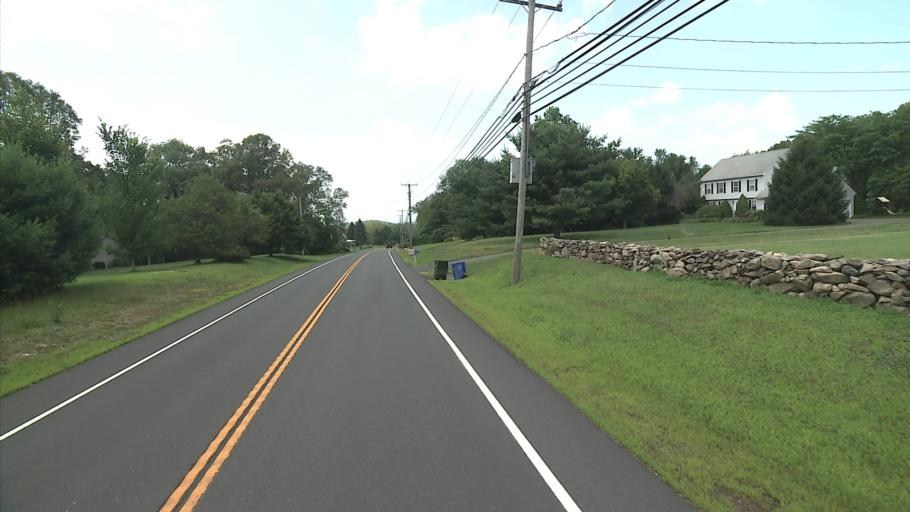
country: US
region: Connecticut
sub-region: Tolland County
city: Rockville
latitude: 41.8445
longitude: -72.4194
